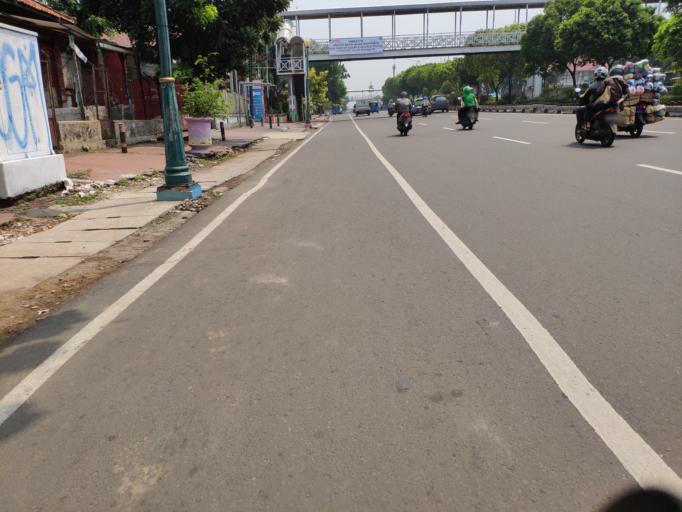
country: ID
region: Jakarta Raya
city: Jakarta
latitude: -6.2067
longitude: 106.8587
